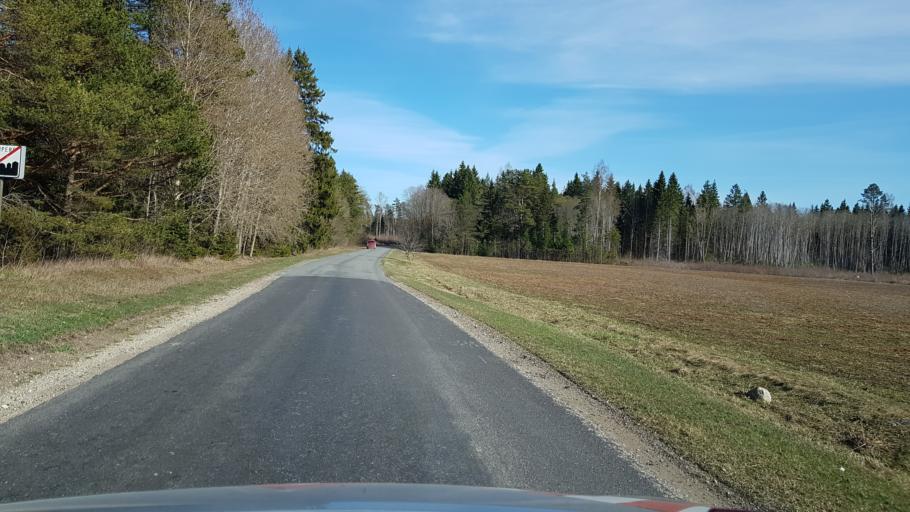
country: EE
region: Harju
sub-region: Nissi vald
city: Riisipere
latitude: 59.0991
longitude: 24.3258
